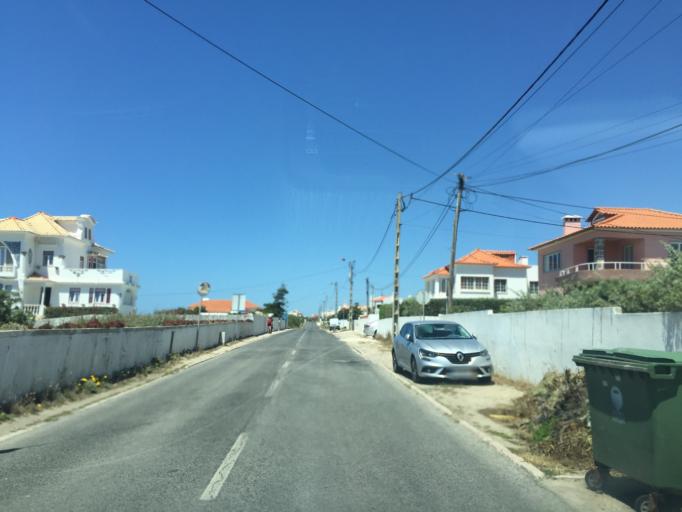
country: PT
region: Lisbon
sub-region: Sintra
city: Colares
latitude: 38.8314
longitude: -9.4676
